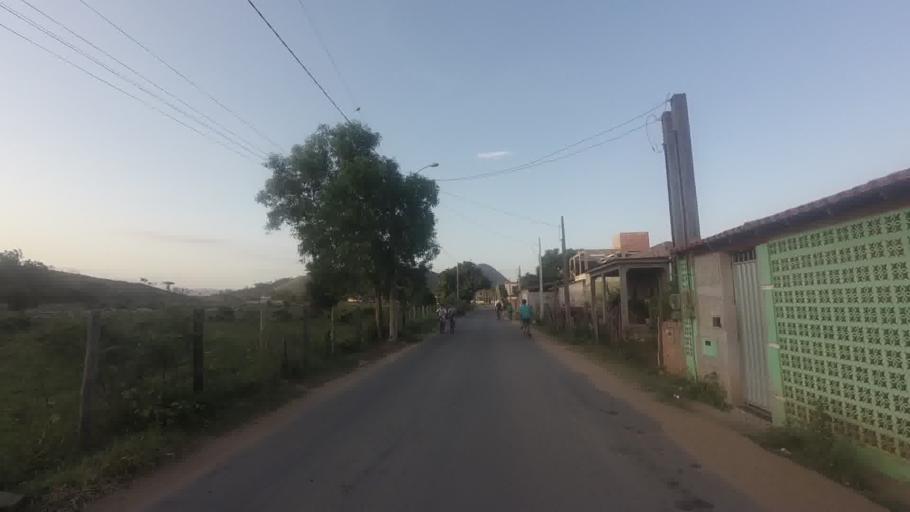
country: BR
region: Espirito Santo
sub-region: Piuma
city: Piuma
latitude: -20.8946
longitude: -40.7846
